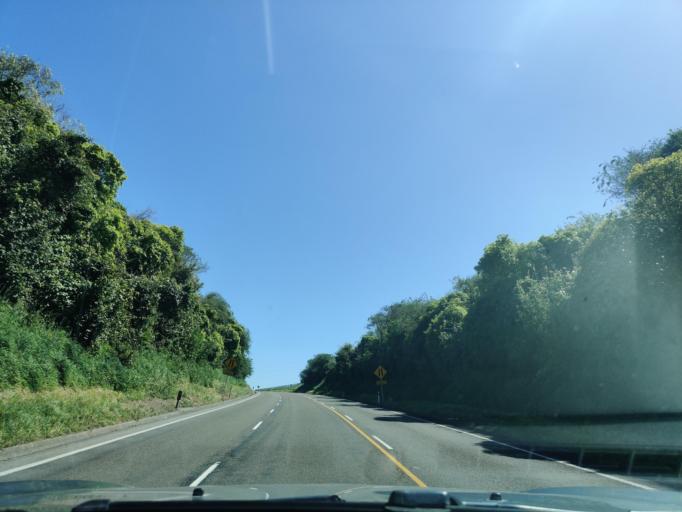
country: NZ
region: Manawatu-Wanganui
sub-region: Wanganui District
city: Wanganui
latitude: -39.8202
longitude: 174.8361
